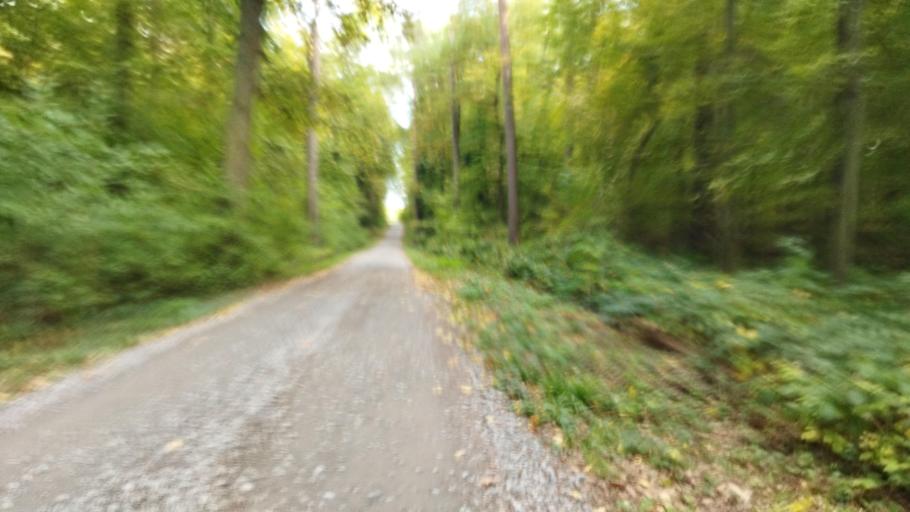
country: DE
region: Baden-Wuerttemberg
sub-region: Karlsruhe Region
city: Sulzfeld
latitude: 49.0973
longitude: 8.8847
